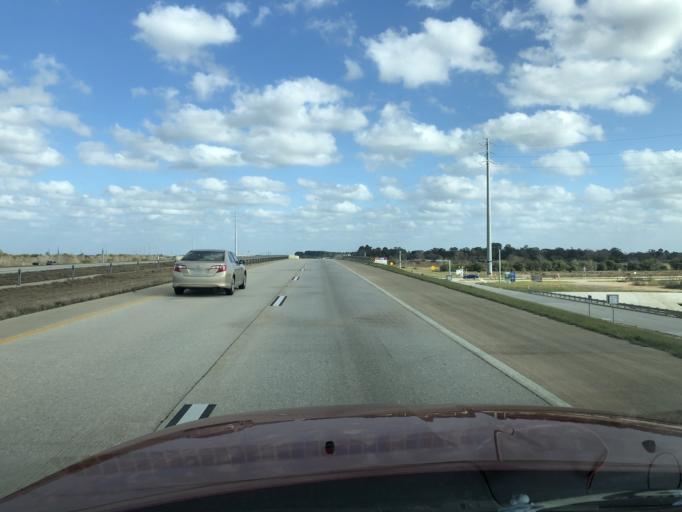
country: US
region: Texas
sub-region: Harris County
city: Cypress
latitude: 30.0533
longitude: -95.7357
